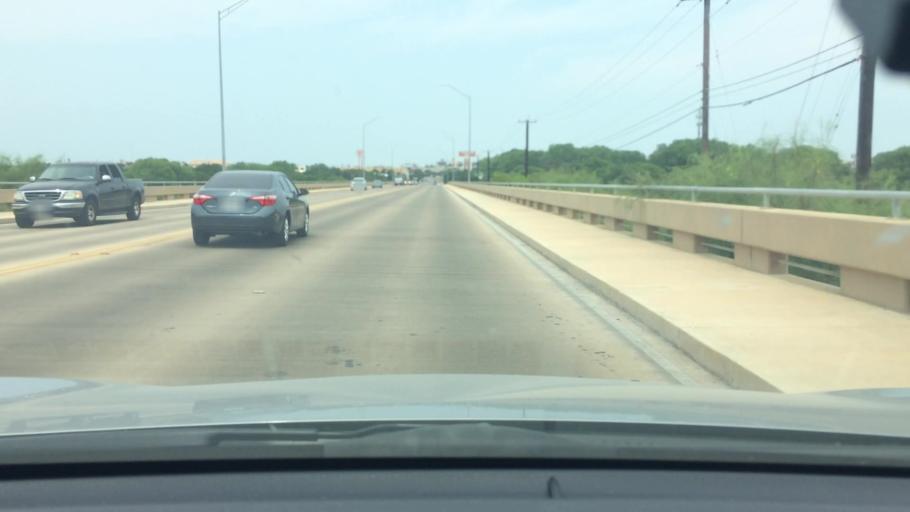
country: US
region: Texas
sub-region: Bexar County
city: Leon Valley
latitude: 29.4624
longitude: -98.6303
